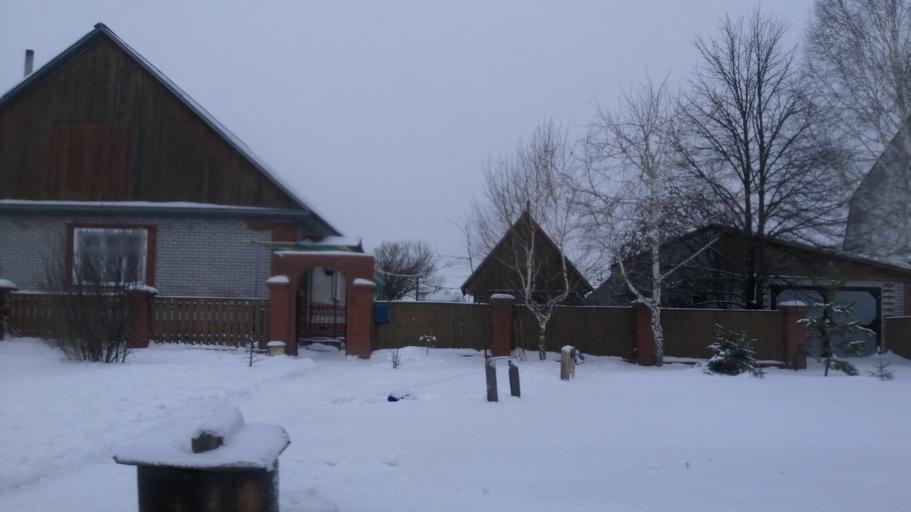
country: RU
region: Novosibirsk
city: Krasnozerskoye
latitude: 53.9925
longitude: 79.2617
